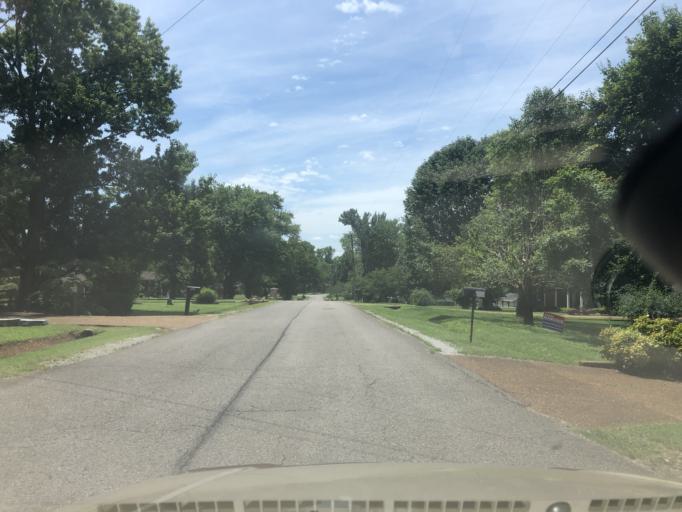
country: US
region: Tennessee
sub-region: Davidson County
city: Lakewood
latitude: 36.2430
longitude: -86.6793
